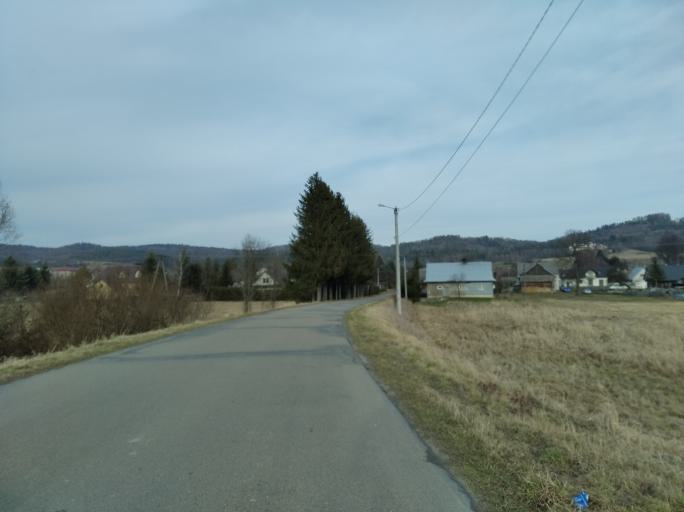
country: PL
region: Subcarpathian Voivodeship
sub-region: Powiat brzozowski
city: Blizne
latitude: 49.7512
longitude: 21.9711
